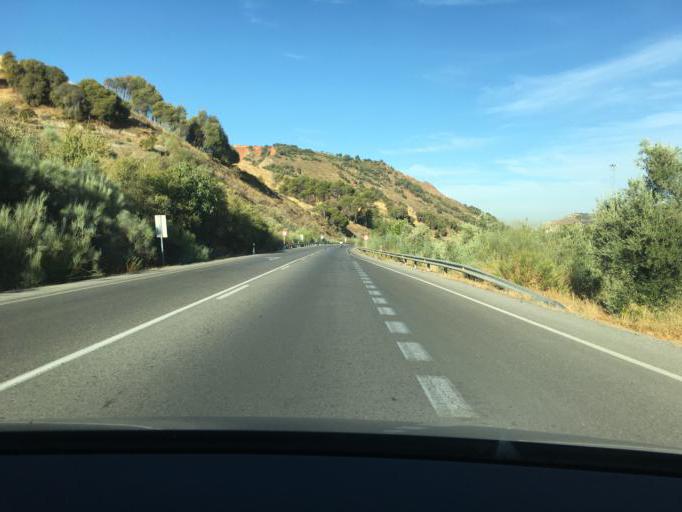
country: ES
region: Andalusia
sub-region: Provincia de Granada
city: Cenes de la Vega
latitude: 37.1540
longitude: -3.5371
